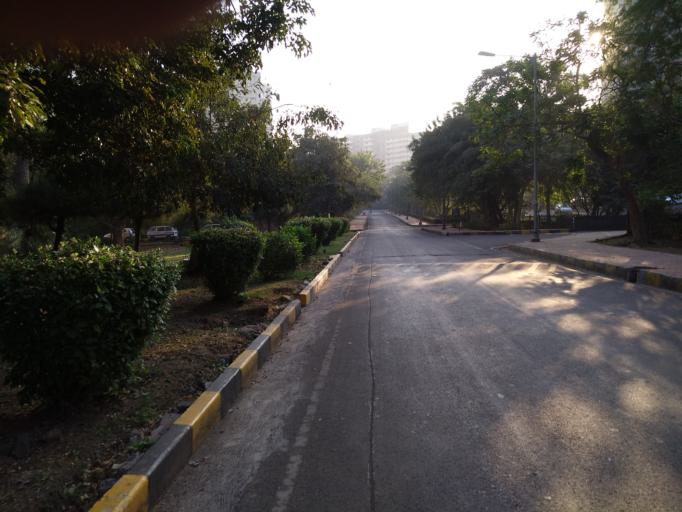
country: IN
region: Maharashtra
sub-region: Mumbai Suburban
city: Mumbai
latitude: 19.0356
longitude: 72.9280
